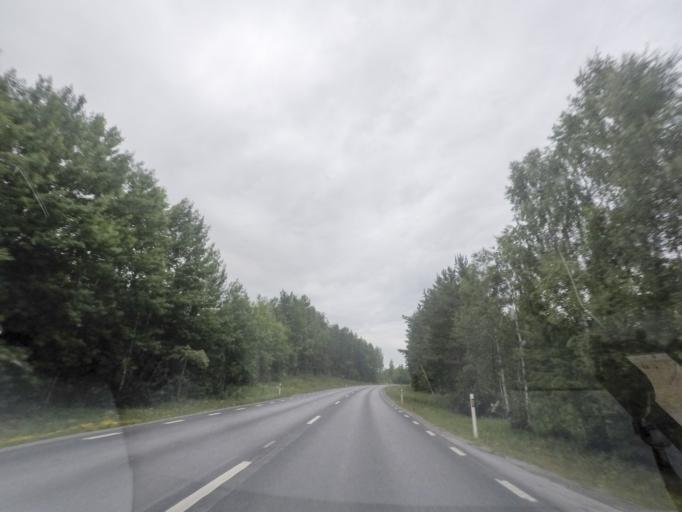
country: SE
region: OErebro
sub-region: Lindesbergs Kommun
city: Lindesberg
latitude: 59.5367
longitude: 15.2582
